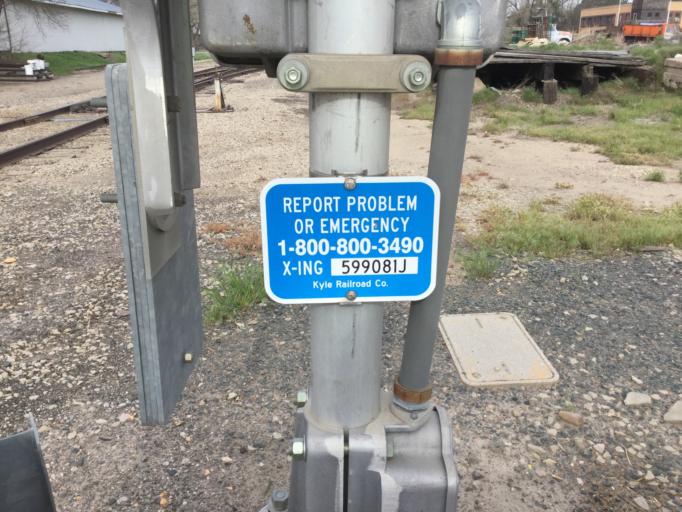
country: US
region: Kansas
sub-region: Norton County
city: Norton
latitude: 39.8273
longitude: -99.8889
